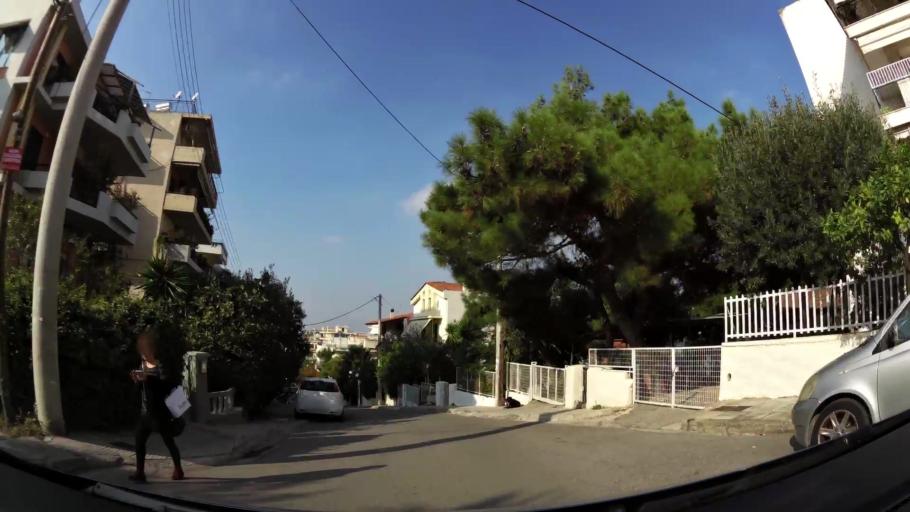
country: GR
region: Attica
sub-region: Nomarchia Athinas
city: Cholargos
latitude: 38.0034
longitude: 23.8069
